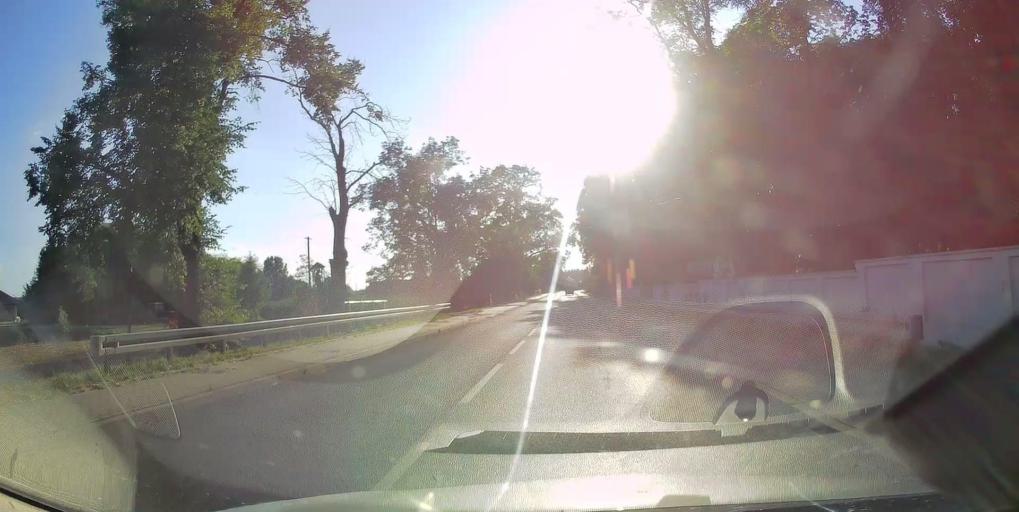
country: PL
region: Lodz Voivodeship
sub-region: Powiat rawski
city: Biala Rawska
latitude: 51.7989
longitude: 20.5291
